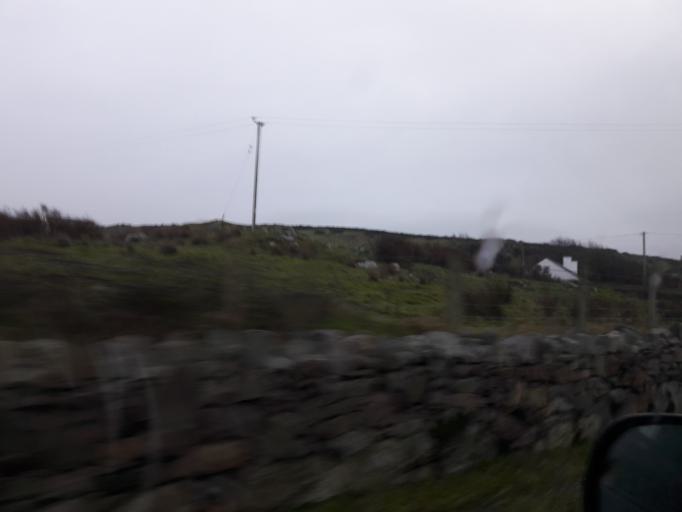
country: IE
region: Ulster
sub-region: County Donegal
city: Ramelton
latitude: 55.2647
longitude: -7.6608
